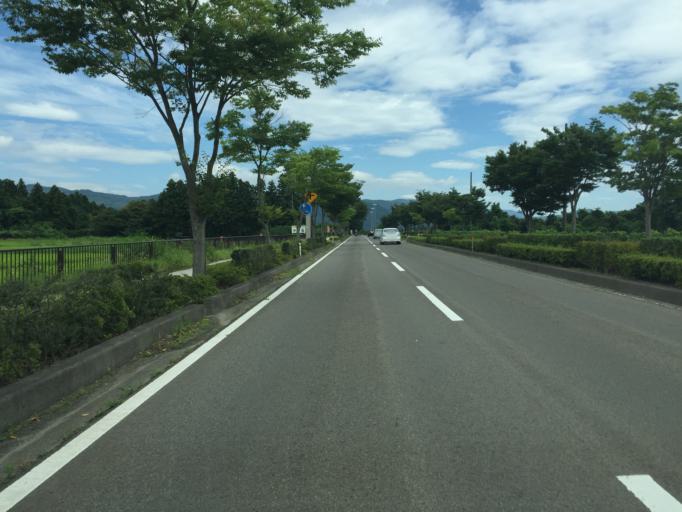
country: JP
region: Fukushima
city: Fukushima-shi
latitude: 37.7500
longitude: 140.3804
